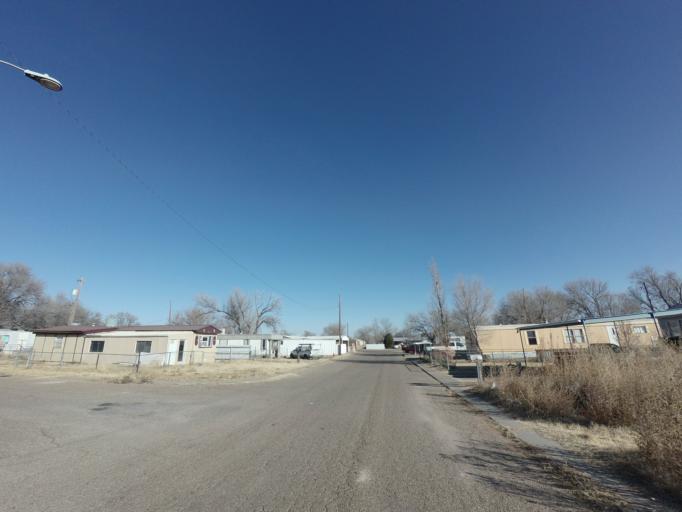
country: US
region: New Mexico
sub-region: Curry County
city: Clovis
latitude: 34.3866
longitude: -103.1993
